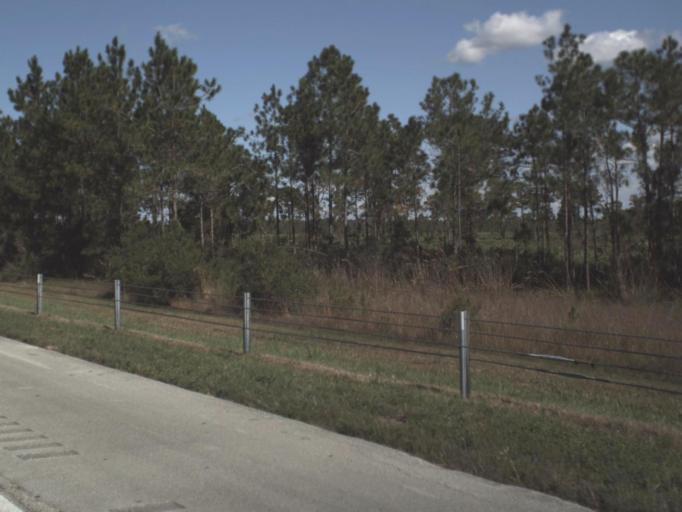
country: US
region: Florida
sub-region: Osceola County
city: Saint Cloud
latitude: 27.9165
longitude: -81.0553
